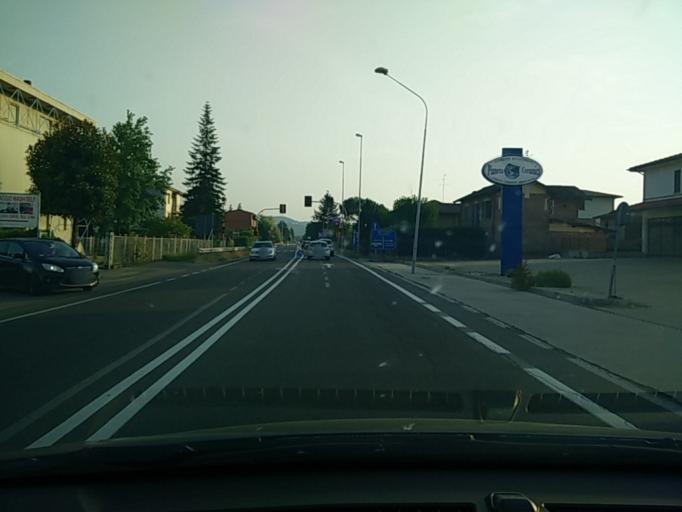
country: IT
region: Lombardy
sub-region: Provincia di Pavia
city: Broni
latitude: 45.0592
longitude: 9.2512
